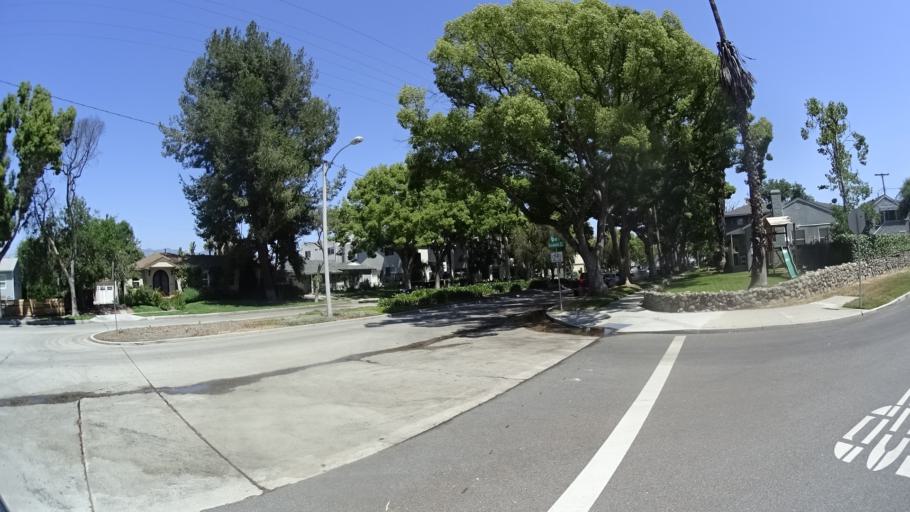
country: US
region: California
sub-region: Los Angeles County
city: North Hollywood
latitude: 34.1764
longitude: -118.3526
